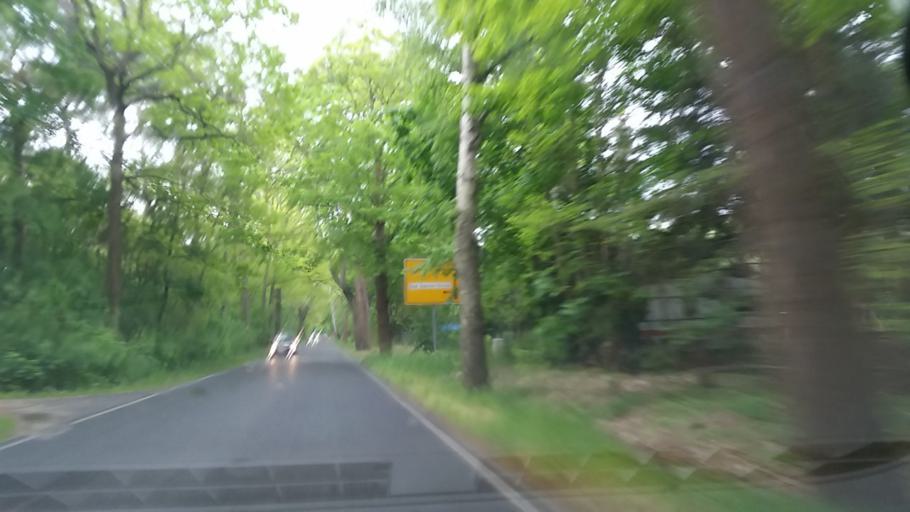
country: DE
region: Brandenburg
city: Diensdorf-Radlow
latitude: 52.2593
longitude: 14.0386
